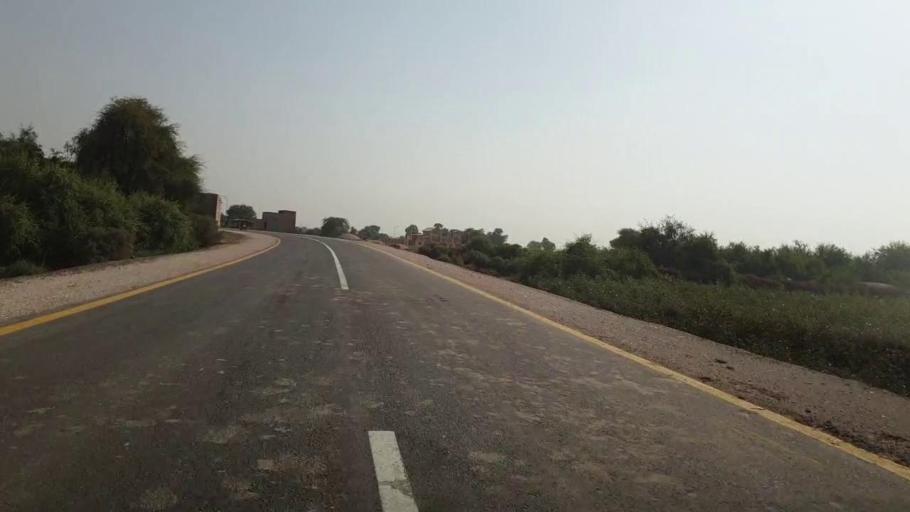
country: PK
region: Sindh
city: Bhan
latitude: 26.5677
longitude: 67.7692
